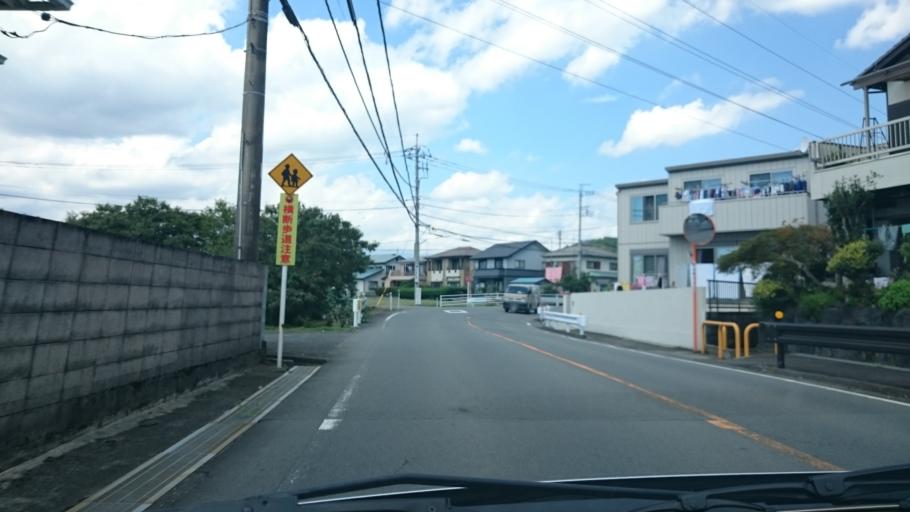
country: JP
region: Shizuoka
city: Gotemba
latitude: 35.2106
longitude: 138.9249
